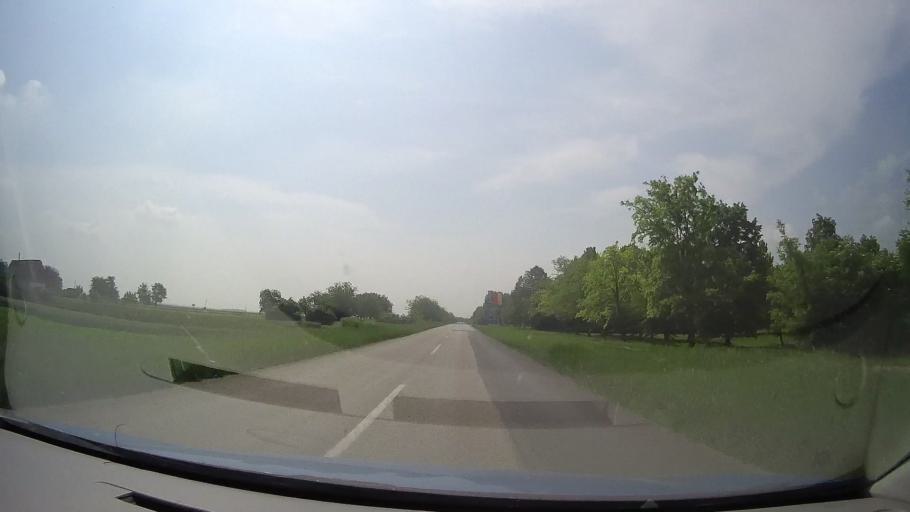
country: RS
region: Autonomna Pokrajina Vojvodina
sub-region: Juznobanatski Okrug
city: Kovacica
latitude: 45.0891
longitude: 20.6350
